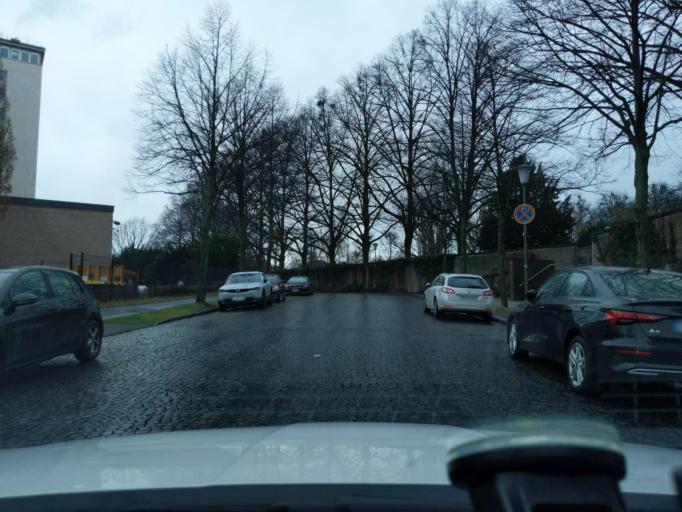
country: DE
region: Hesse
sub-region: Regierungsbezirk Kassel
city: Kassel
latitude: 51.3168
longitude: 9.4596
